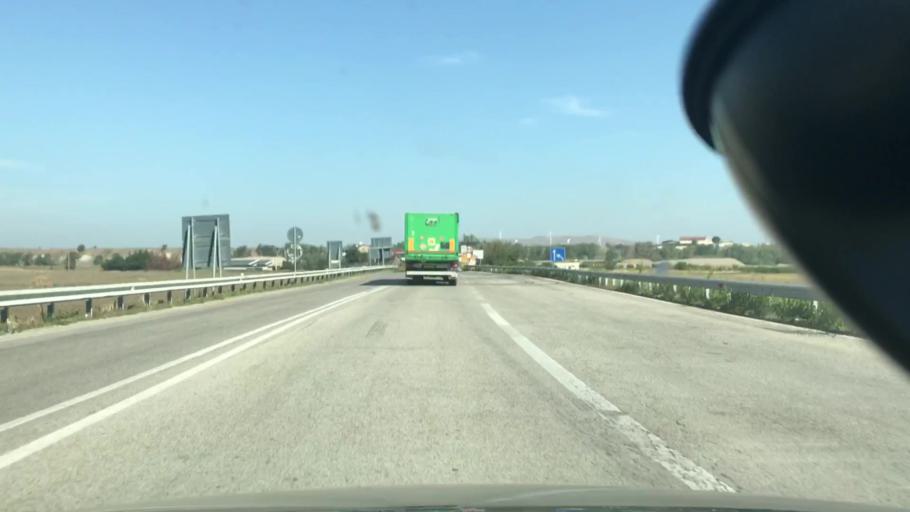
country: IT
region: Basilicate
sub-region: Provincia di Potenza
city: Zona 179
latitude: 41.0905
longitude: 15.5954
